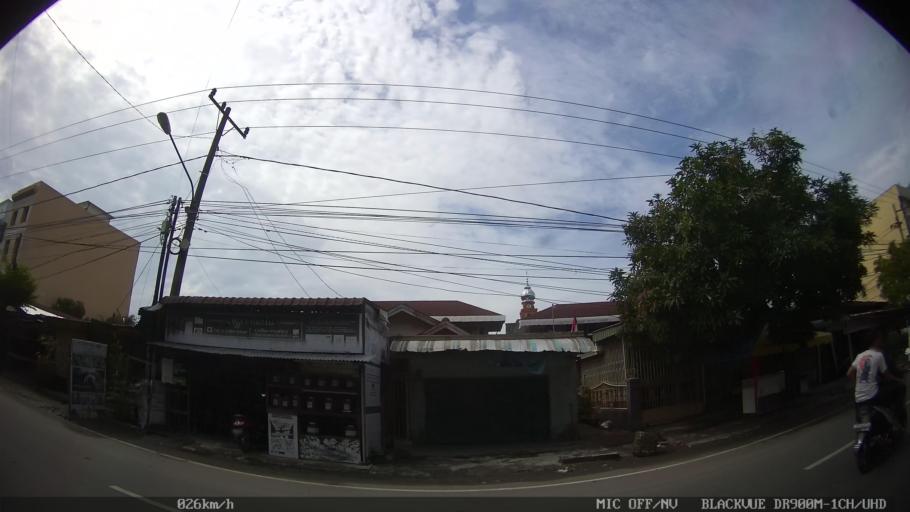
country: ID
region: North Sumatra
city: Medan
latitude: 3.6225
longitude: 98.6959
